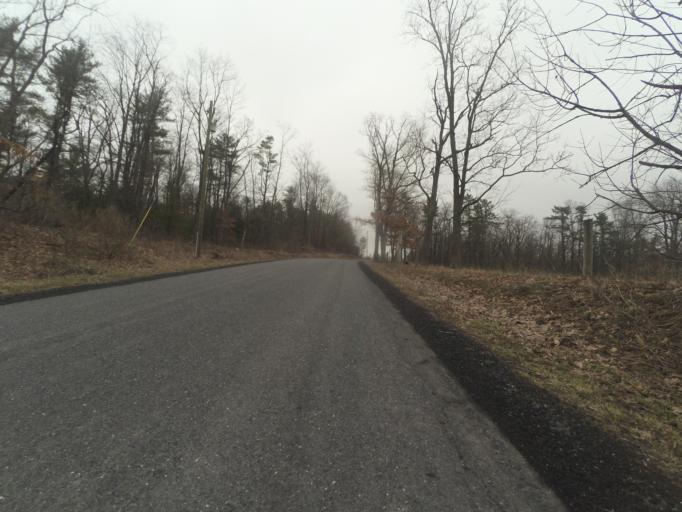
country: US
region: Pennsylvania
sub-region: Centre County
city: Centre Hall
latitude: 40.8717
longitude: -77.6223
